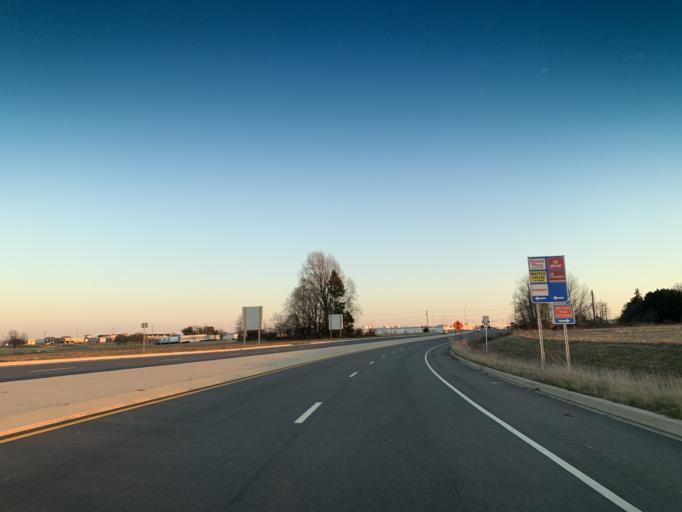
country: US
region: Delaware
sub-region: New Castle County
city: Middletown
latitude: 39.4434
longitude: -75.7494
